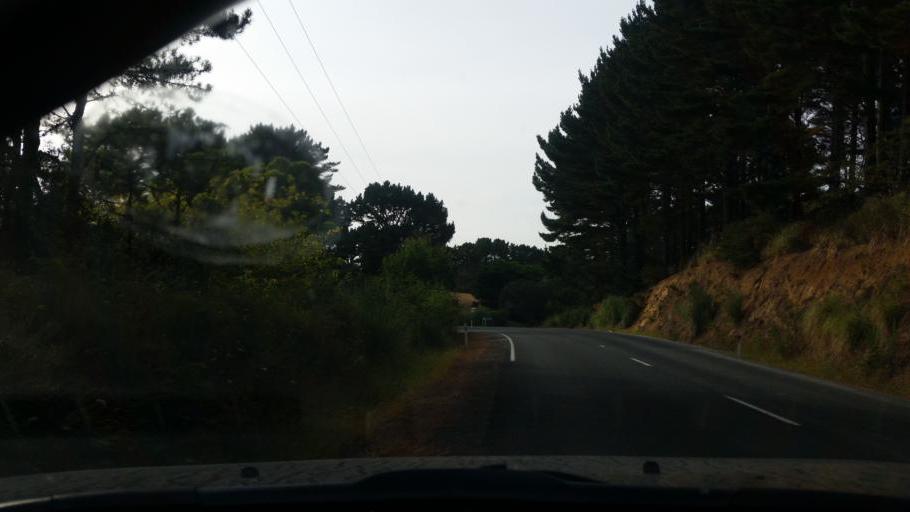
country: NZ
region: Northland
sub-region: Kaipara District
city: Dargaville
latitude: -36.2168
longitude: 174.0355
